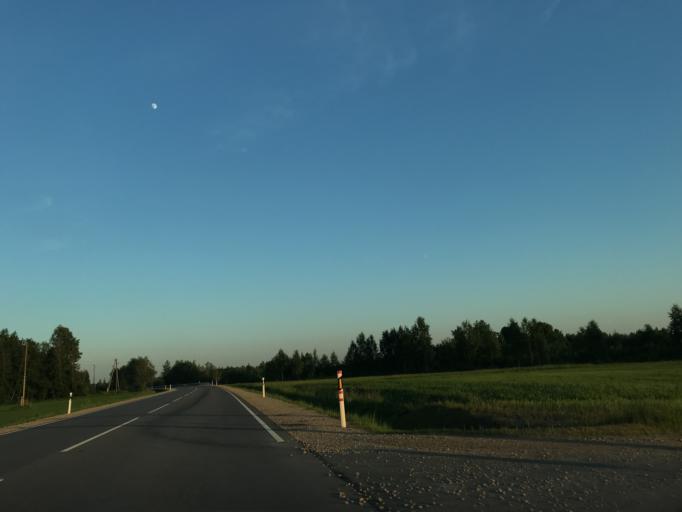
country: LV
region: Jaunjelgava
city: Jaunjelgava
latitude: 56.4047
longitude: 24.9329
